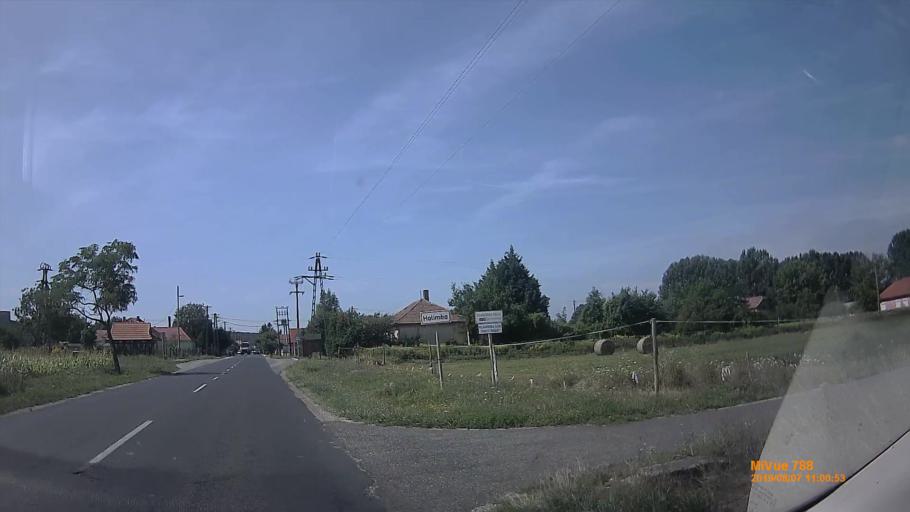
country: HU
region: Veszprem
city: Ajka
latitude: 47.0380
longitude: 17.5389
